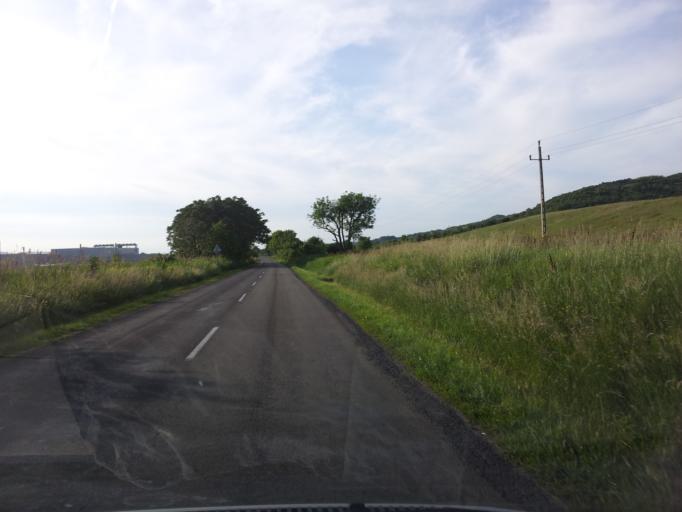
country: HU
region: Komarom-Esztergom
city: Esztergom
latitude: 47.7632
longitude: 18.7612
